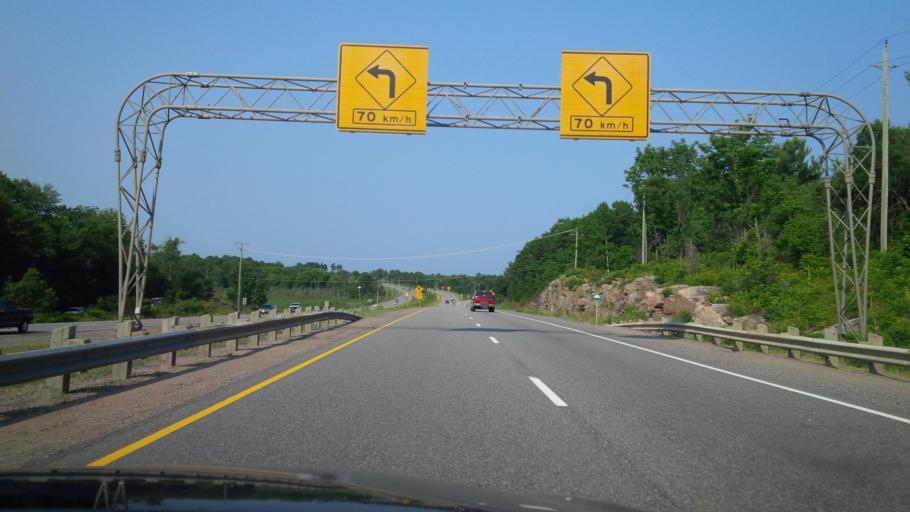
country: CA
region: Ontario
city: Gravenhurst
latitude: 44.9084
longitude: -79.3560
